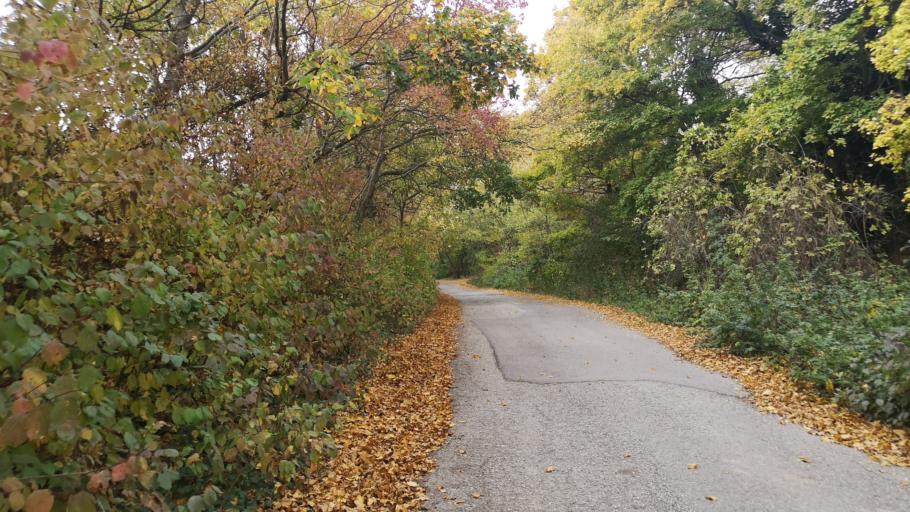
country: SK
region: Nitriansky
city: Cachtice
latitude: 48.7152
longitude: 17.7755
